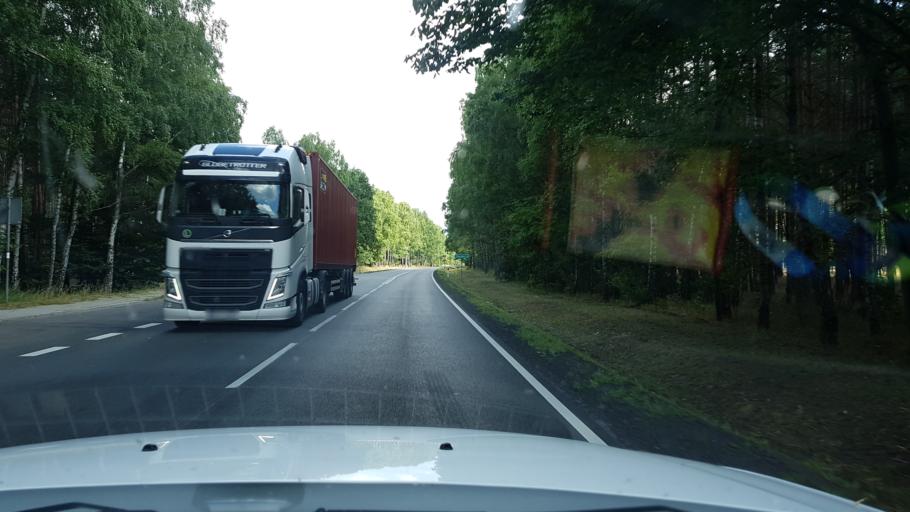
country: PL
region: West Pomeranian Voivodeship
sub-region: Powiat walecki
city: Walcz
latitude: 53.3116
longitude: 16.3701
